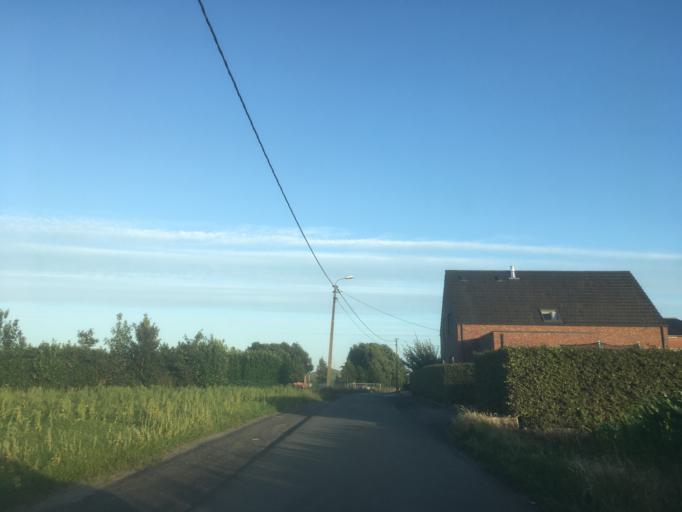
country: BE
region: Flanders
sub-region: Provincie West-Vlaanderen
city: Torhout
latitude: 51.0576
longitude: 3.0800
